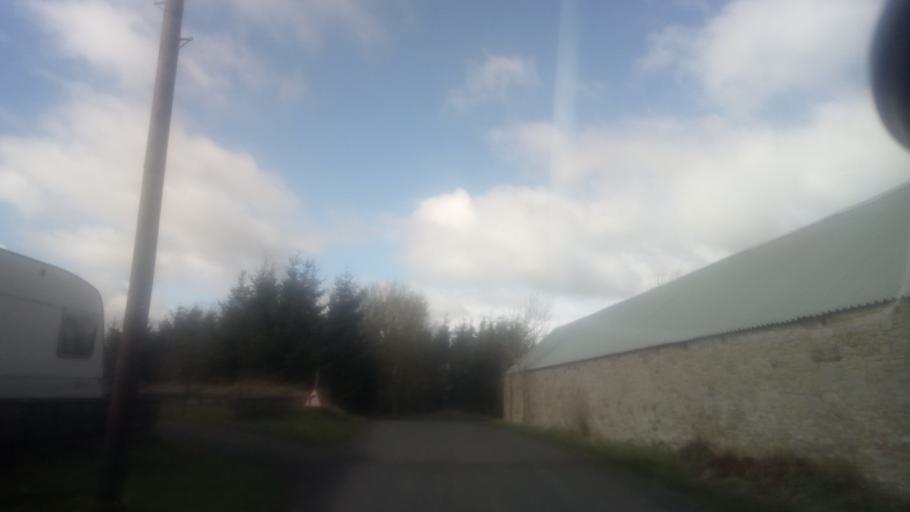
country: GB
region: Scotland
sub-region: The Scottish Borders
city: Jedburgh
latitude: 55.4737
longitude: -2.6146
